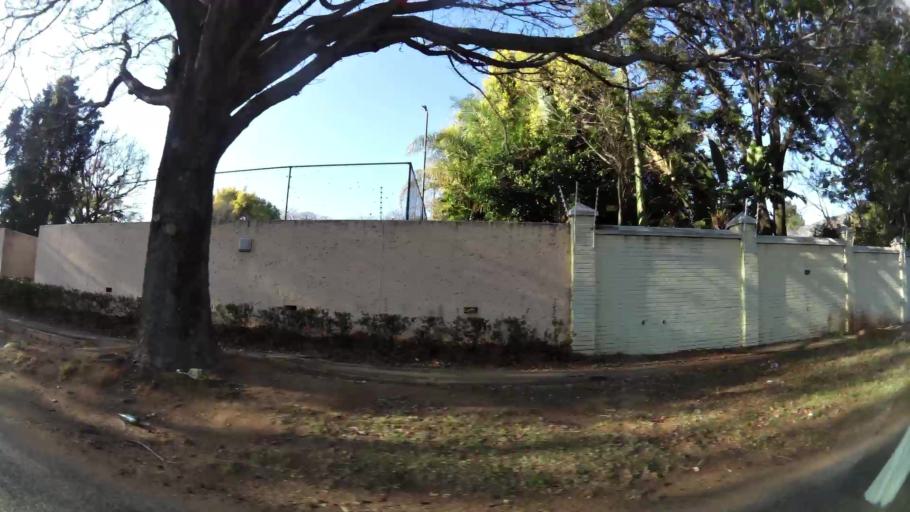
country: ZA
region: Gauteng
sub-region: City of Johannesburg Metropolitan Municipality
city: Johannesburg
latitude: -26.1374
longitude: 28.0742
